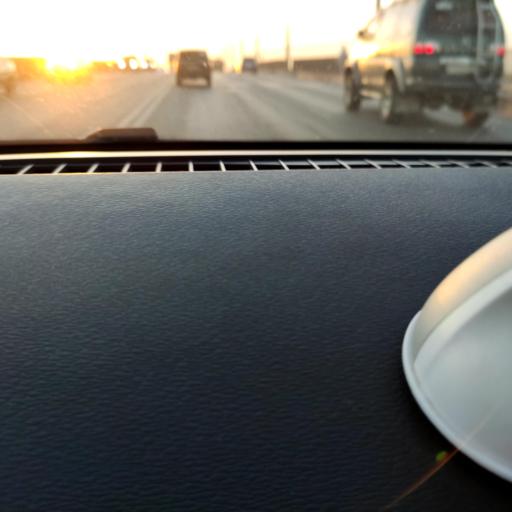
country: RU
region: Samara
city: Petra-Dubrava
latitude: 53.2554
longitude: 50.3034
